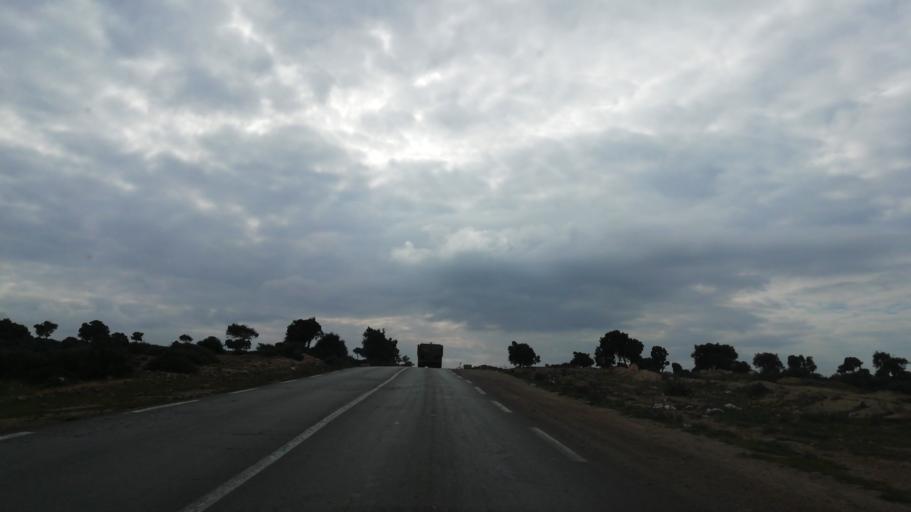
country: DZ
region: Oran
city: Ain el Bya
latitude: 35.7312
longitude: -0.3549
